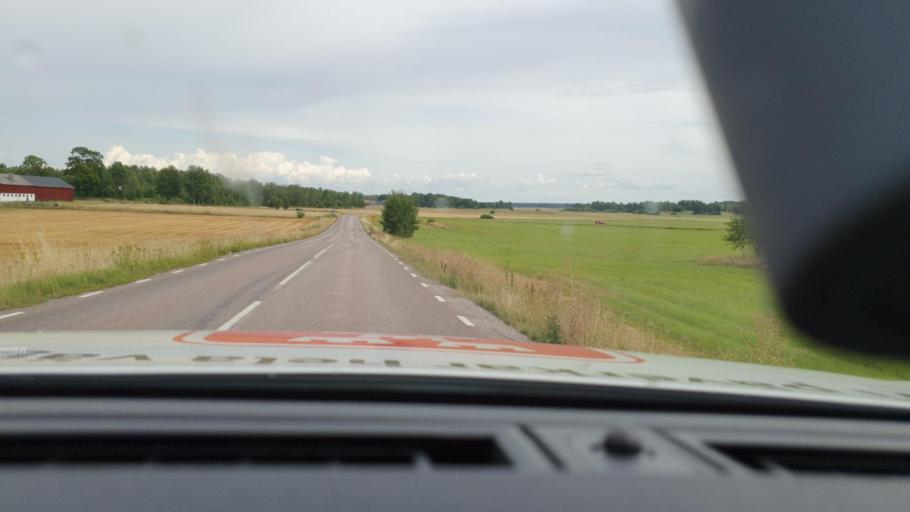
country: SE
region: Uppsala
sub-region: Heby Kommun
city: OEstervala
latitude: 60.0969
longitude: 17.1811
